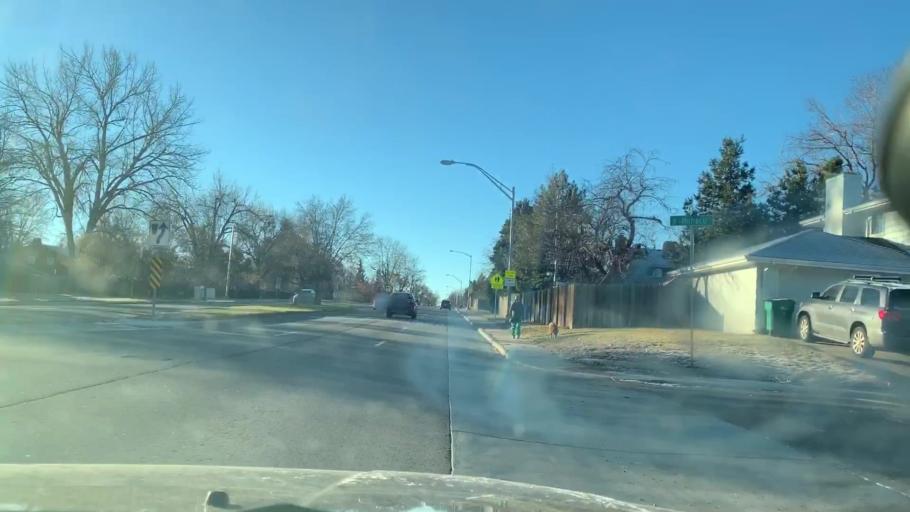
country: US
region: Colorado
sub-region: Arapahoe County
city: Cherry Hills Village
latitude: 39.6596
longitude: -104.9130
